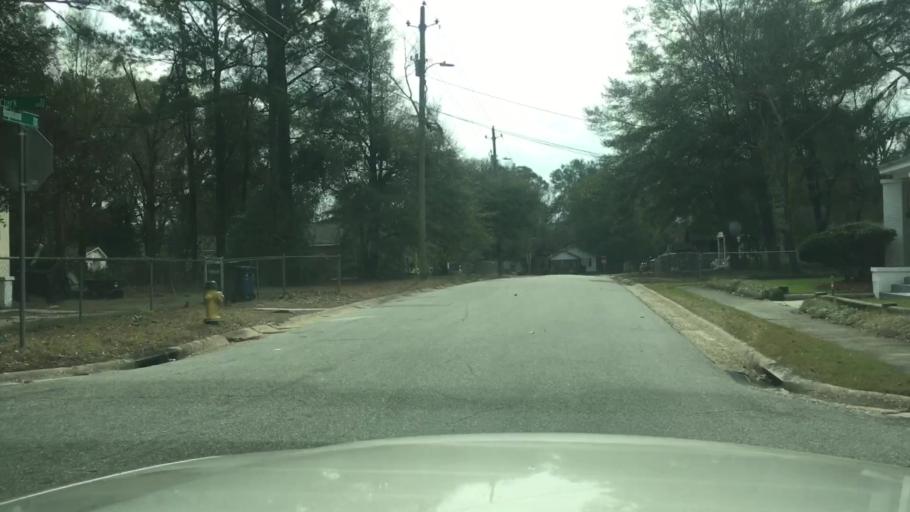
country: US
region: North Carolina
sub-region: Cumberland County
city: Fayetteville
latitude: 35.0541
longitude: -78.8993
